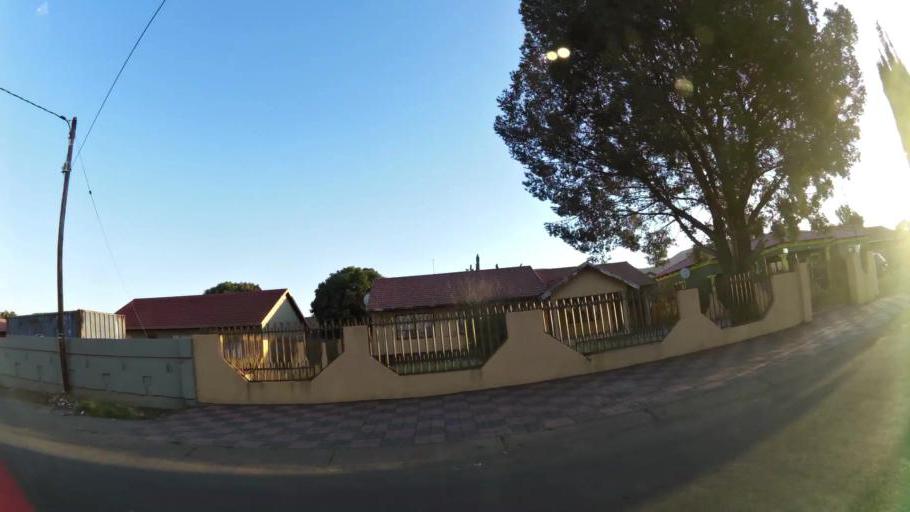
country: ZA
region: North-West
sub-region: Bojanala Platinum District Municipality
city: Rustenburg
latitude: -25.6367
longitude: 27.2075
